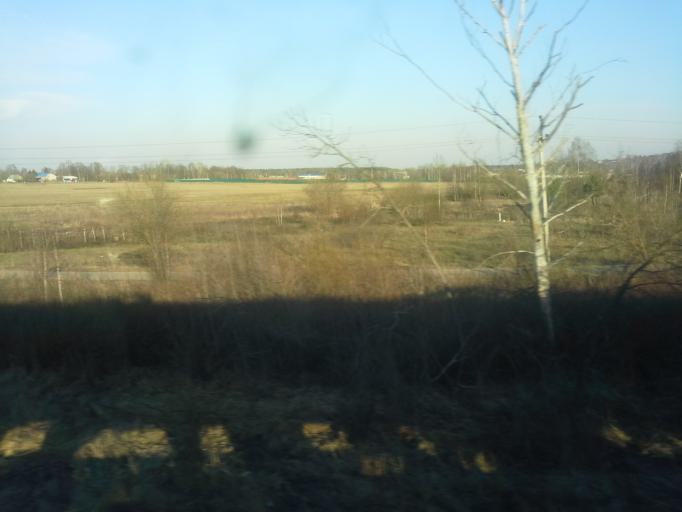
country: RU
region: Moskovskaya
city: Nekrasovskiy
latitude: 56.0816
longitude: 37.4998
